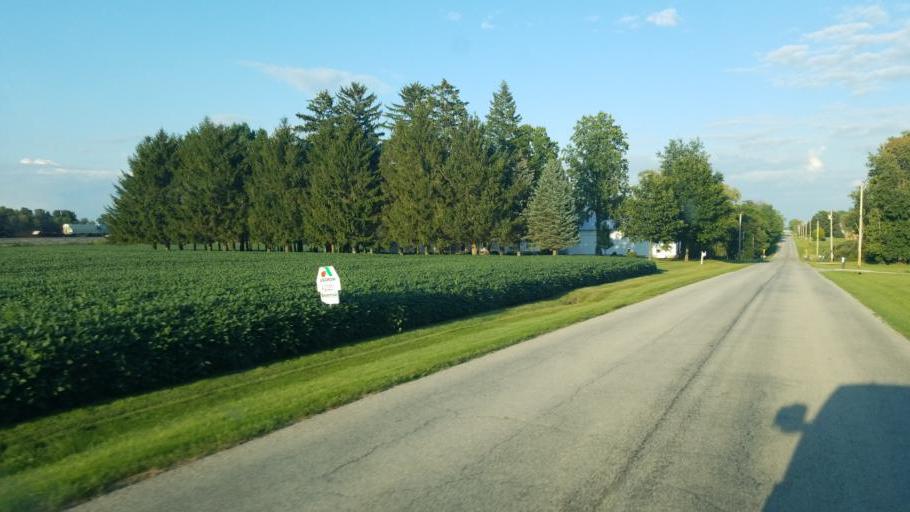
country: US
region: Ohio
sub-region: Huron County
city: Plymouth
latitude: 41.0523
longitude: -82.6520
